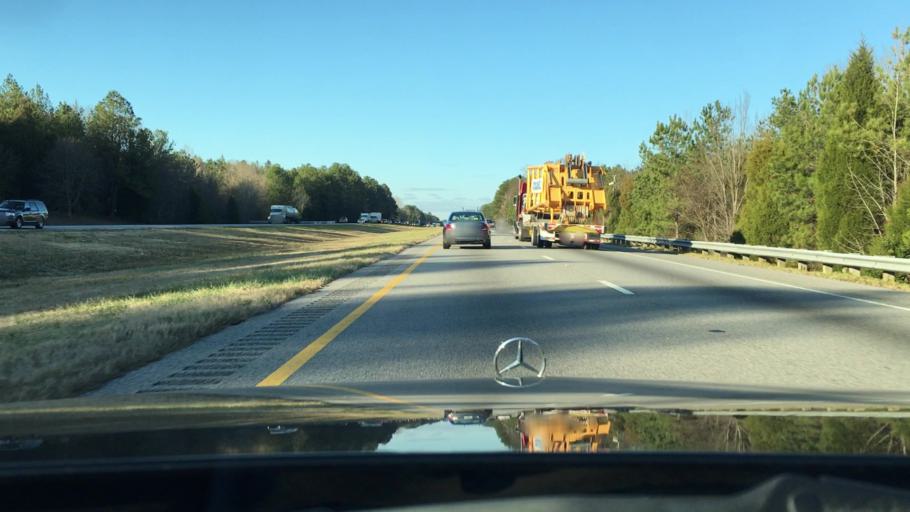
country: US
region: South Carolina
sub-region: Chester County
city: Great Falls
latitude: 34.6698
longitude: -81.0290
